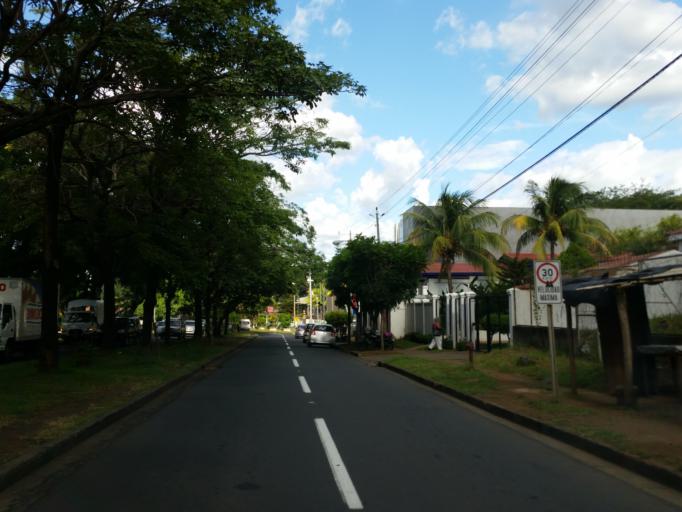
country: NI
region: Managua
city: Managua
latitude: 12.1025
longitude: -86.2653
